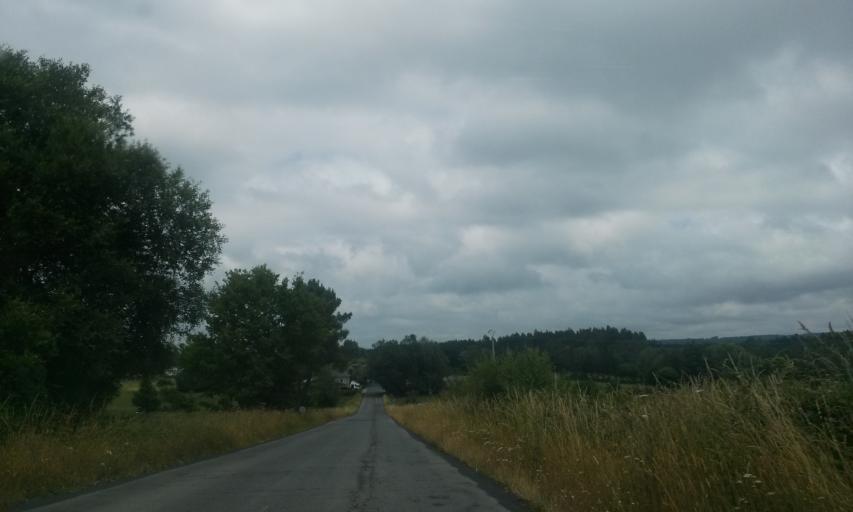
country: ES
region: Galicia
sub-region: Provincia de Lugo
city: Friol
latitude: 43.0895
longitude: -7.8096
